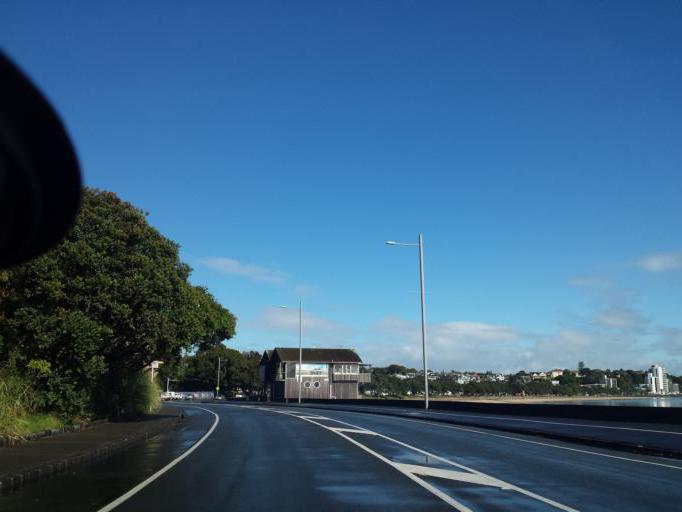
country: NZ
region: Auckland
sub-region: Auckland
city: Tamaki
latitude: -36.8502
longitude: 174.8493
